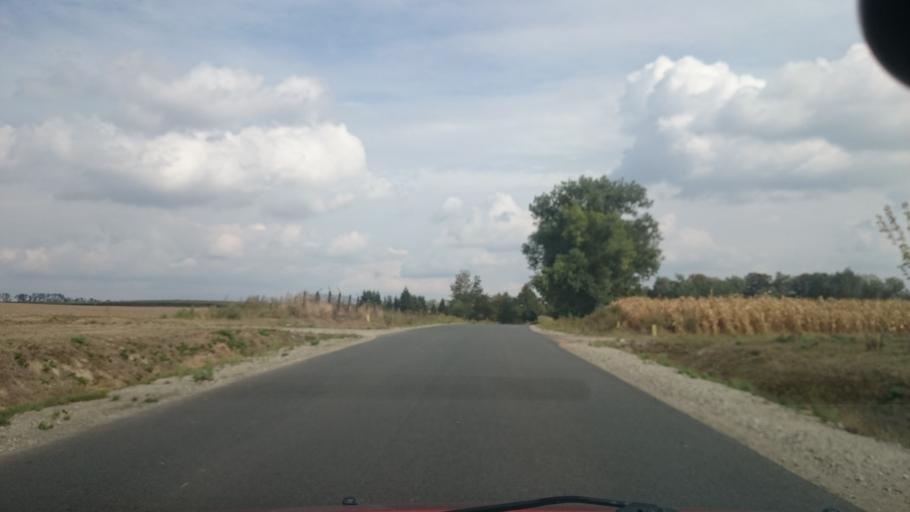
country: PL
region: Opole Voivodeship
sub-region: Powiat nyski
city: Nysa
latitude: 50.4865
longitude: 17.2738
